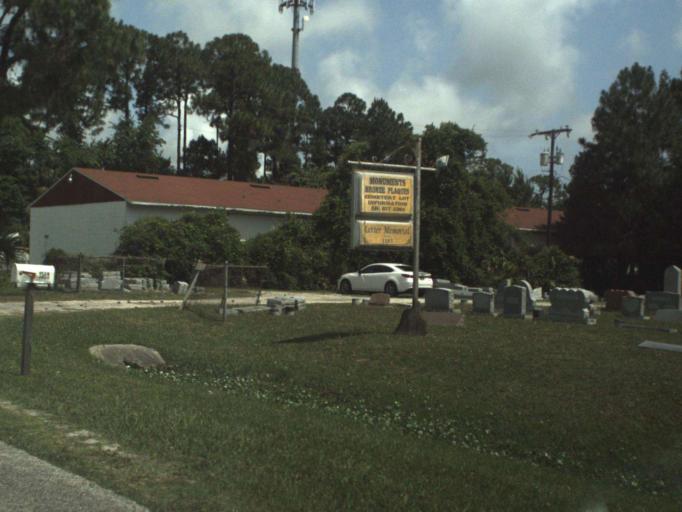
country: US
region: Florida
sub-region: Volusia County
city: Ormond-by-the-Sea
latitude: 29.3169
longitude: -81.1065
